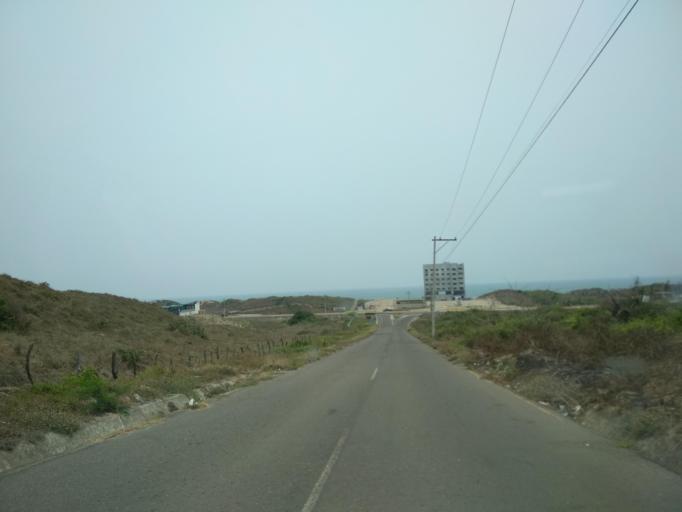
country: MX
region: Veracruz
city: Anton Lizardo
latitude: 19.0507
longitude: -96.0309
